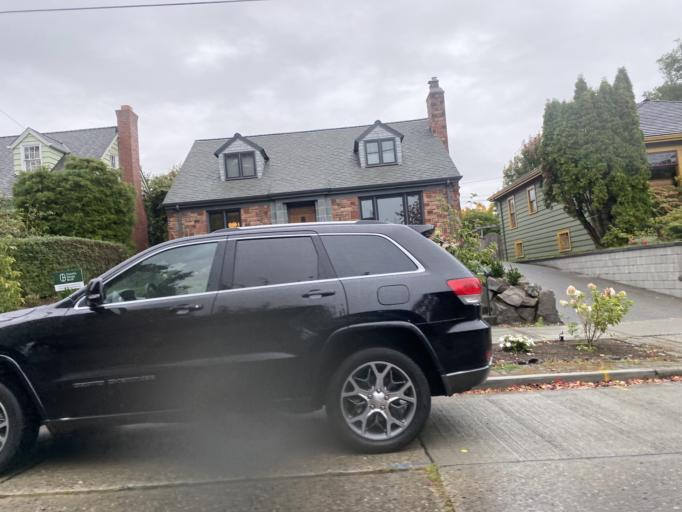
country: US
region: Washington
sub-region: King County
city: Seattle
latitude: 47.6442
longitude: -122.3930
